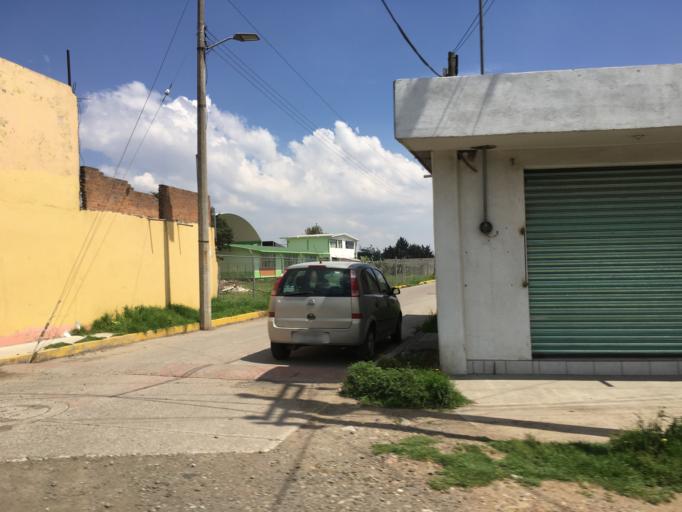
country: MX
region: Mexico
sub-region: Timilpan
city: Tercera Manzana de Zaragoza
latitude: 19.8749
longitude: -99.6873
